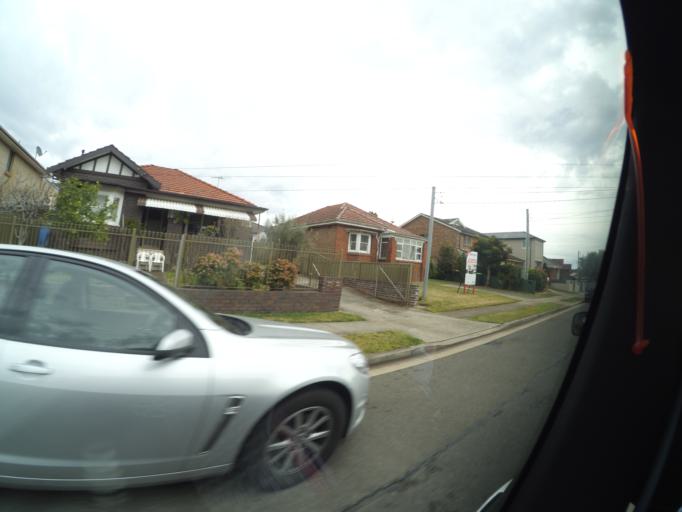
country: AU
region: New South Wales
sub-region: Bankstown
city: Bankstown
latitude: -33.9190
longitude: 151.0261
